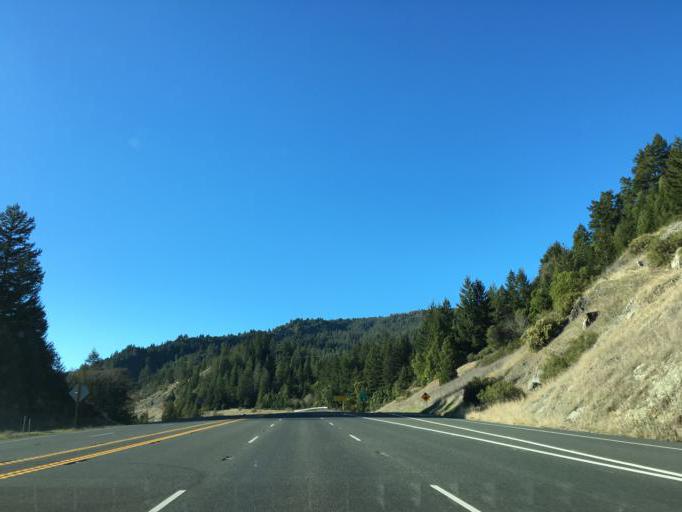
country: US
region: California
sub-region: Mendocino County
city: Laytonville
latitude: 39.8338
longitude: -123.6286
